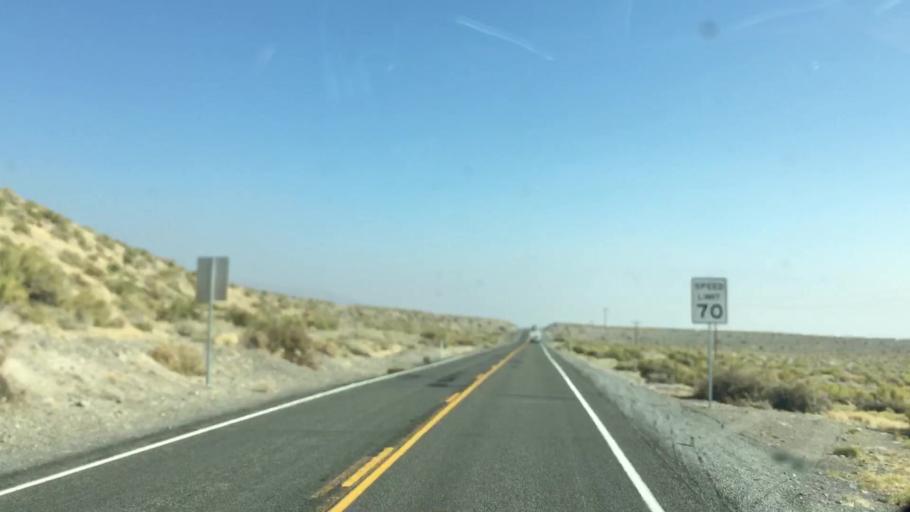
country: US
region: Nevada
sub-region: Lyon County
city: Fernley
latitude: 40.1654
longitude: -119.3684
